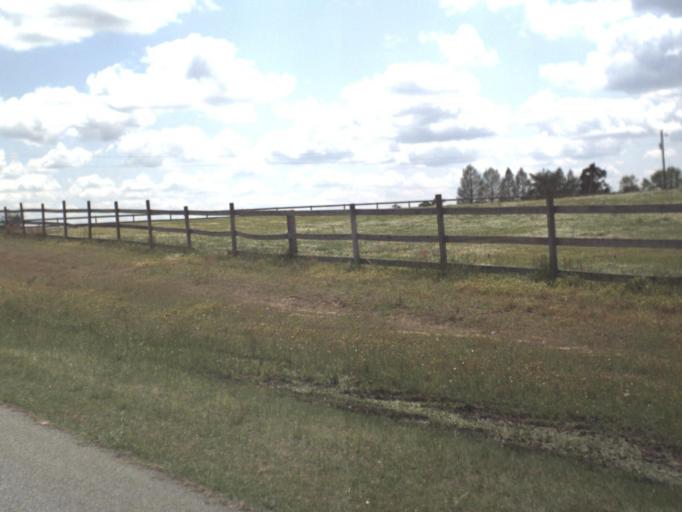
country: US
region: Florida
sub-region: Escambia County
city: Molino
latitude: 30.8073
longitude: -87.4246
